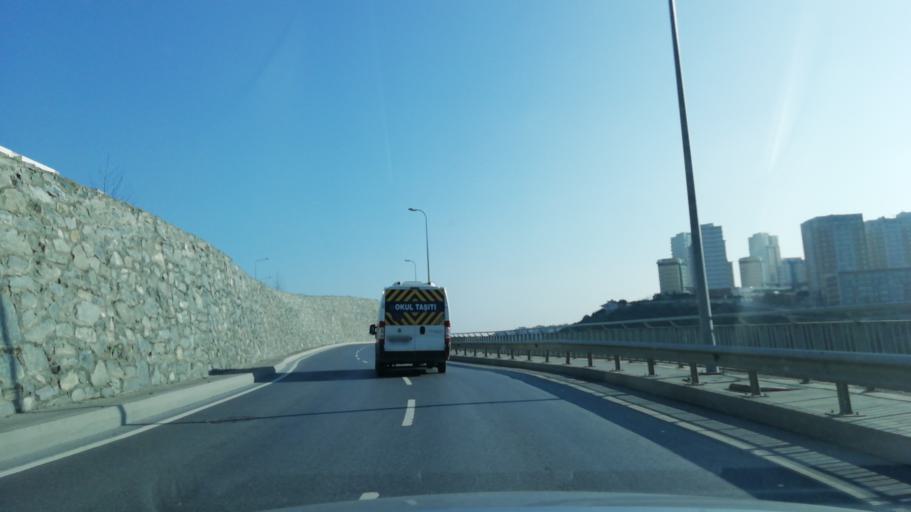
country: TR
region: Istanbul
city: Esenyurt
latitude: 41.0784
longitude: 28.6878
